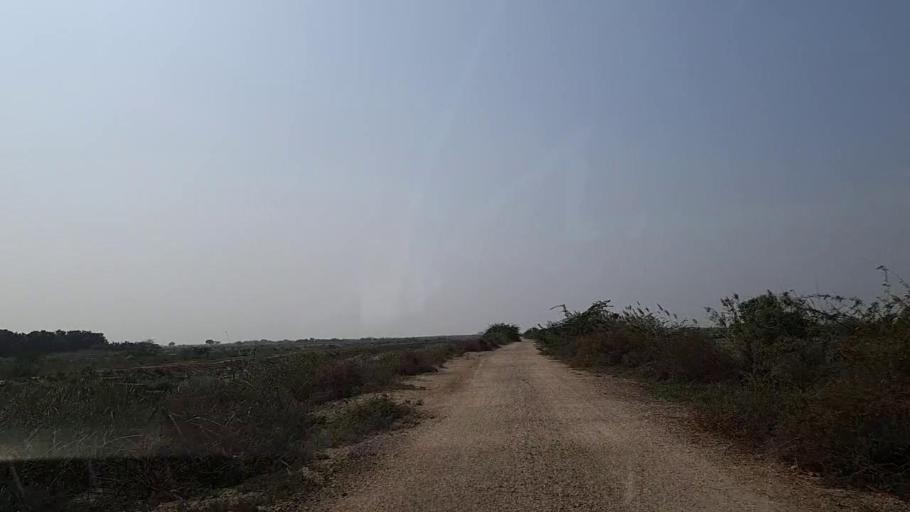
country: PK
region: Sindh
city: Gharo
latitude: 24.6834
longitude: 67.7427
